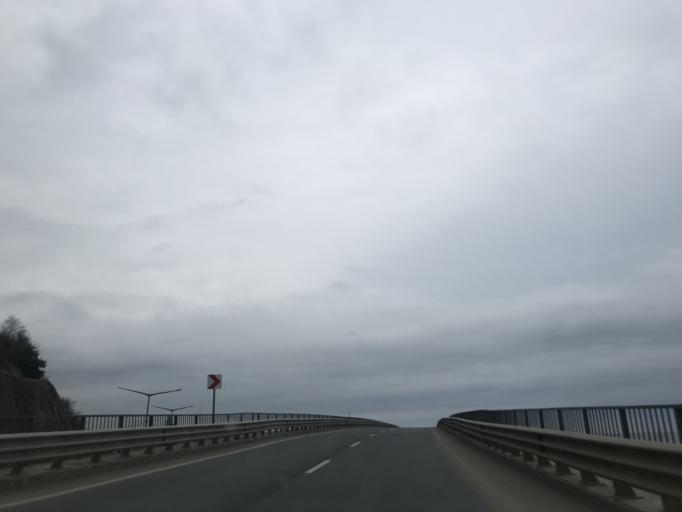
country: TR
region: Trabzon
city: Akcaabat
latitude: 41.0017
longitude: 39.6364
